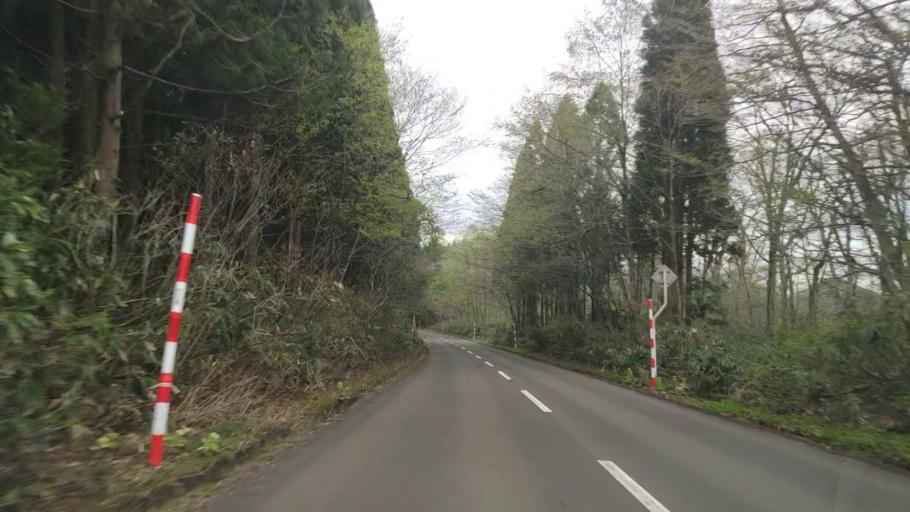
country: JP
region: Akita
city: Hanawa
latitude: 40.3943
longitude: 140.7959
